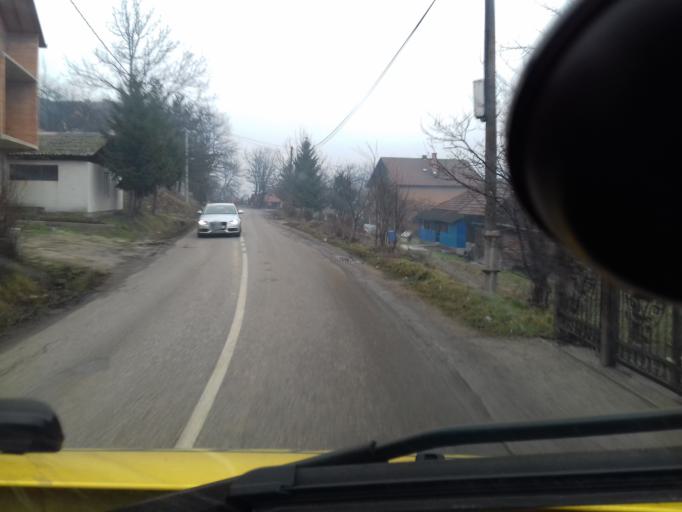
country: BA
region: Federation of Bosnia and Herzegovina
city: Lokvine
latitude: 44.2045
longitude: 17.8587
